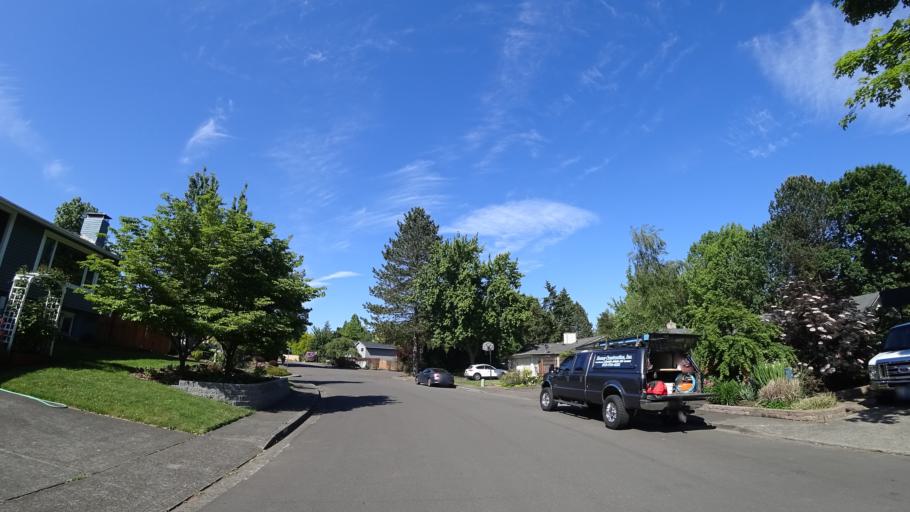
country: US
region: Oregon
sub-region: Washington County
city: Beaverton
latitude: 45.4552
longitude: -122.8029
